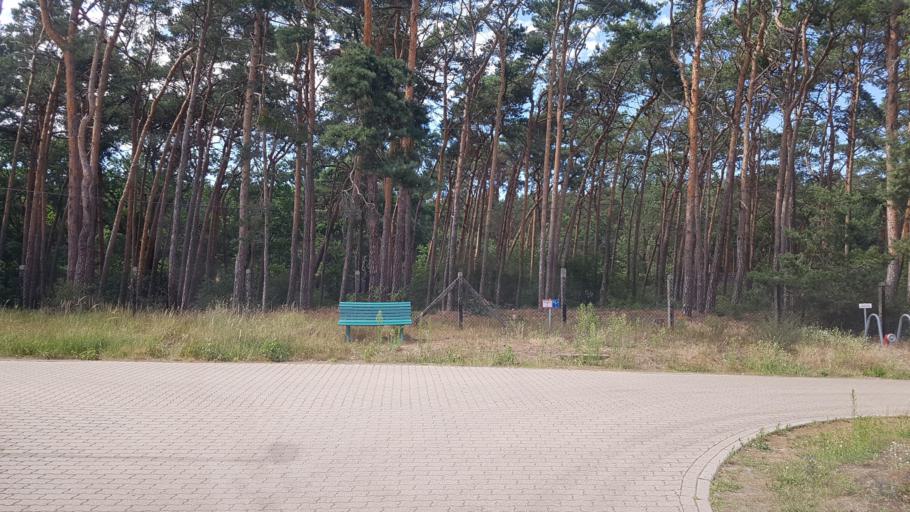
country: DE
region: Brandenburg
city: Luckenwalde
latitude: 52.1136
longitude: 13.1845
